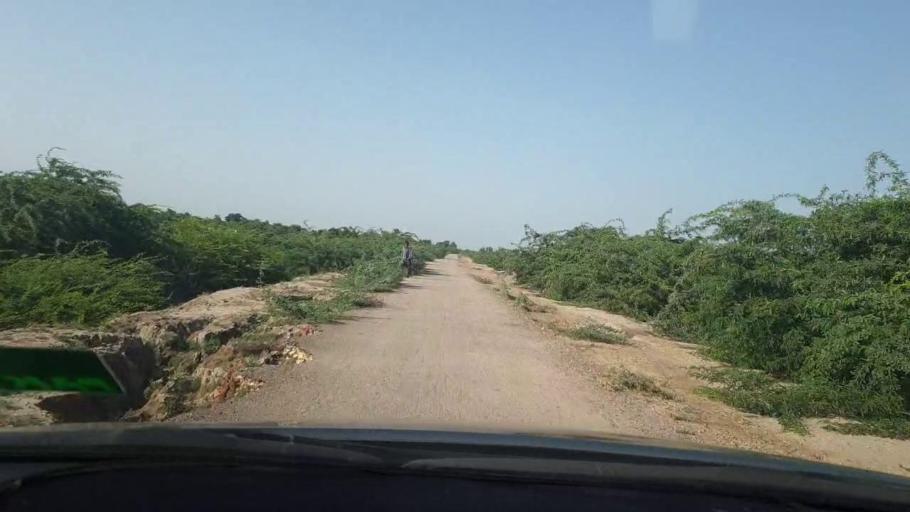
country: PK
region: Sindh
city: Naukot
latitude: 24.8632
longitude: 69.3181
